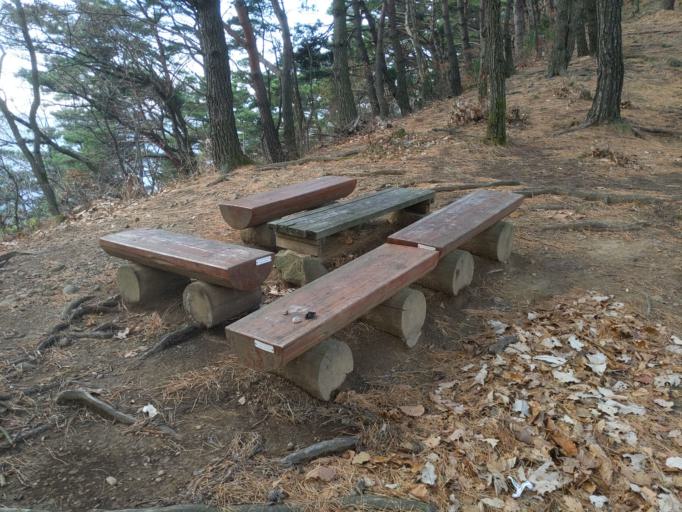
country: KR
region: Daegu
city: Hwawon
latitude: 35.7798
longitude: 128.5515
